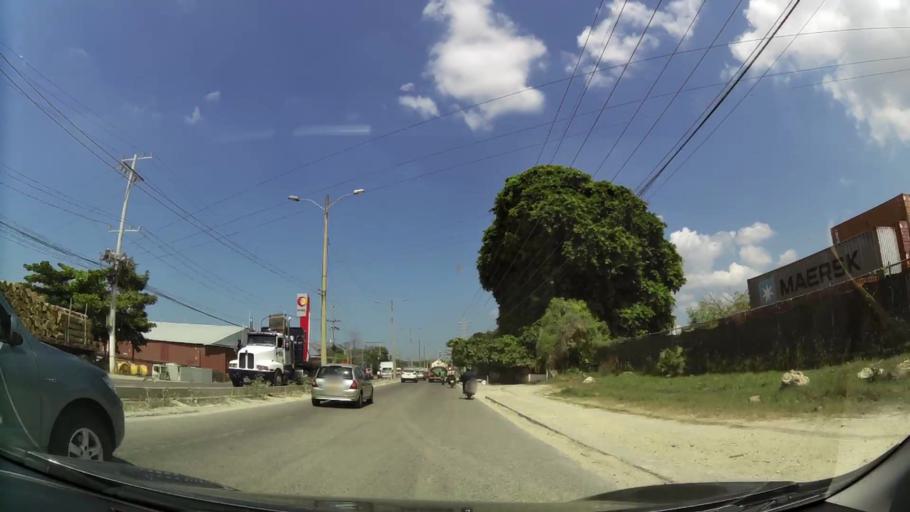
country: CO
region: Bolivar
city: Cartagena
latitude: 10.3642
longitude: -75.5078
